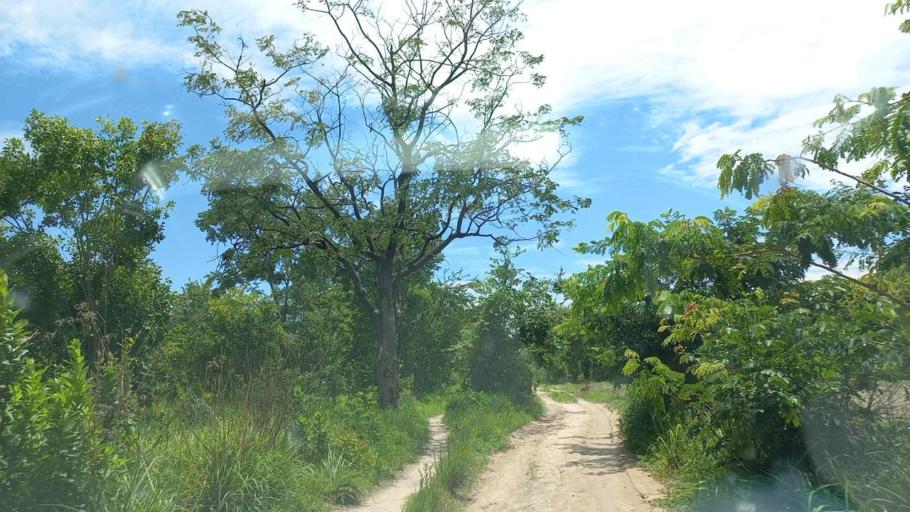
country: ZM
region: Copperbelt
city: Ndola
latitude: -12.8735
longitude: 28.4447
